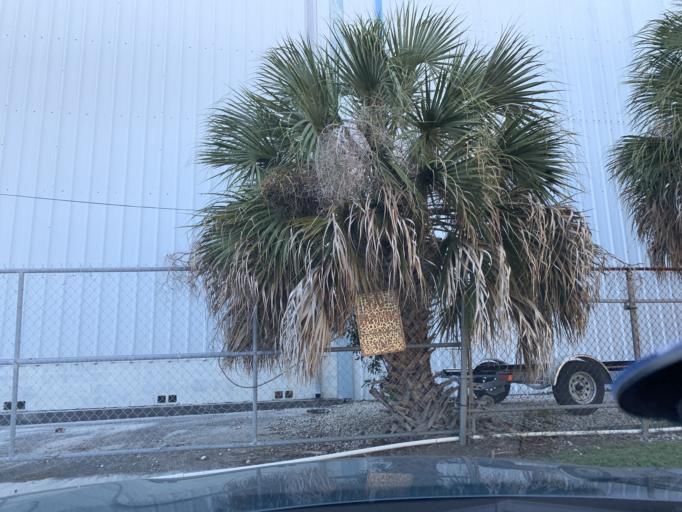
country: US
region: Florida
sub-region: Pinellas County
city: Gulfport
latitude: 27.7384
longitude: -82.7011
